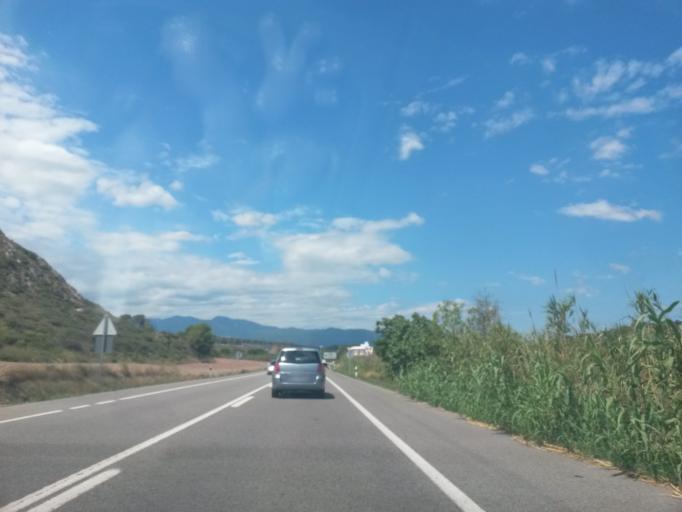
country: ES
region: Catalonia
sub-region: Provincia de Girona
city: Biure
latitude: 42.3470
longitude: 2.9122
